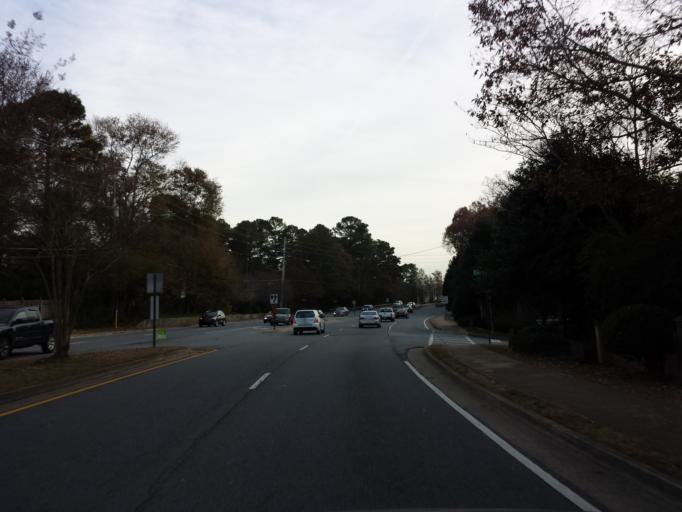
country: US
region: Georgia
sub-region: Fulton County
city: Roswell
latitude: 33.9892
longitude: -84.4272
